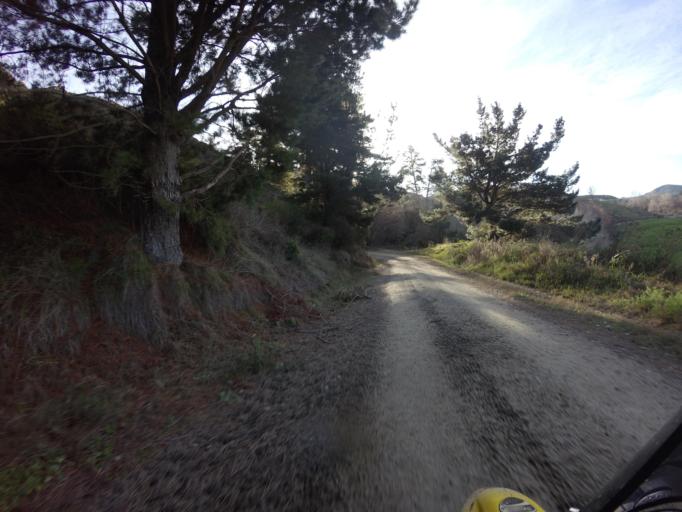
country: NZ
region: Hawke's Bay
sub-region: Wairoa District
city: Wairoa
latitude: -38.7409
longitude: 177.5188
